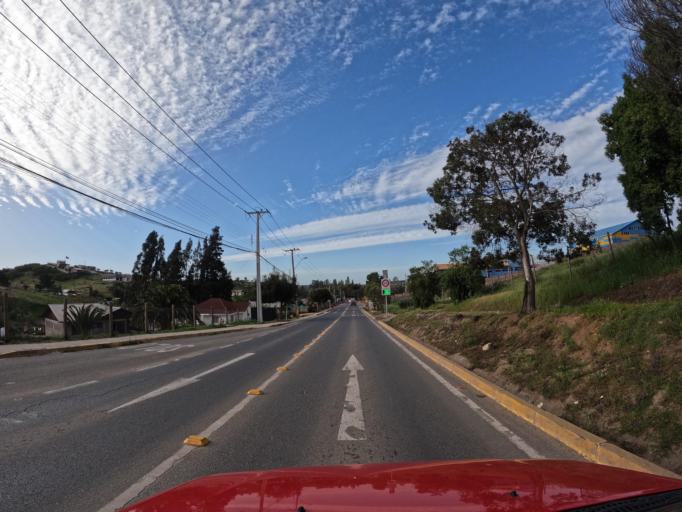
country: CL
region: Valparaiso
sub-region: San Antonio Province
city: San Antonio
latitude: -34.1265
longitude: -71.7269
